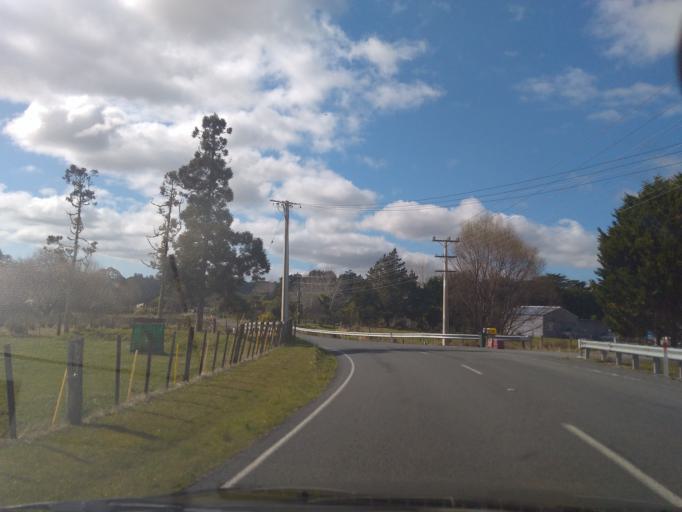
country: NZ
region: Northland
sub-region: Whangarei
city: Whangarei
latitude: -35.7009
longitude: 174.3490
